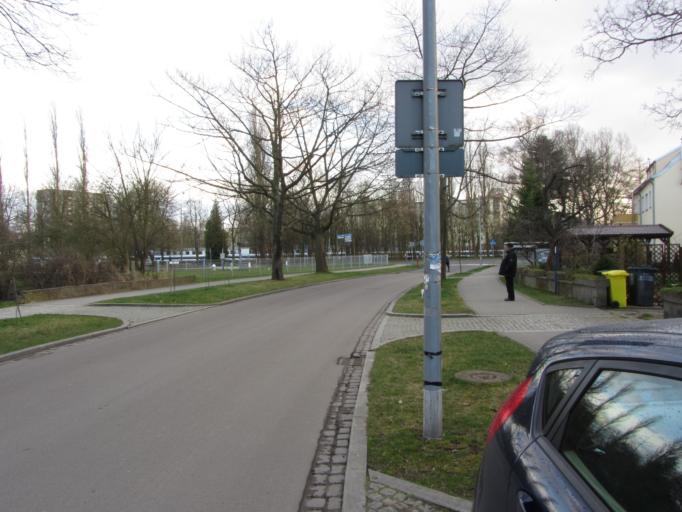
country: PL
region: West Pomeranian Voivodeship
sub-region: Powiat kolobrzeski
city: Kolobrzeg
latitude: 54.1831
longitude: 15.5799
